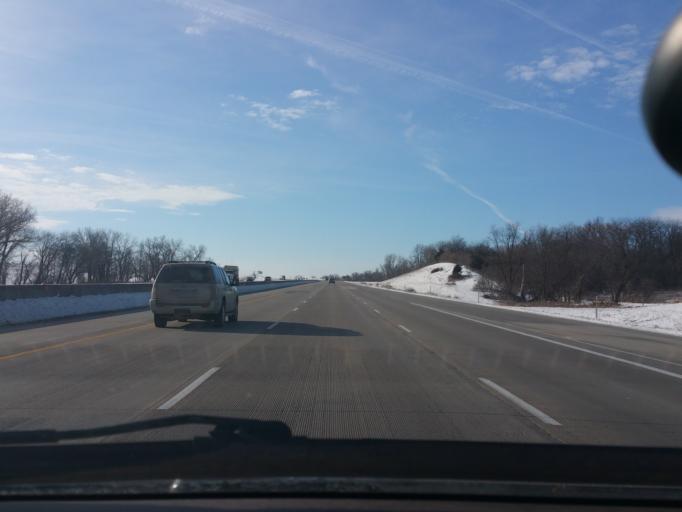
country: US
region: Iowa
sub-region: Polk County
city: West Des Moines
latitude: 41.5191
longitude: -93.7753
